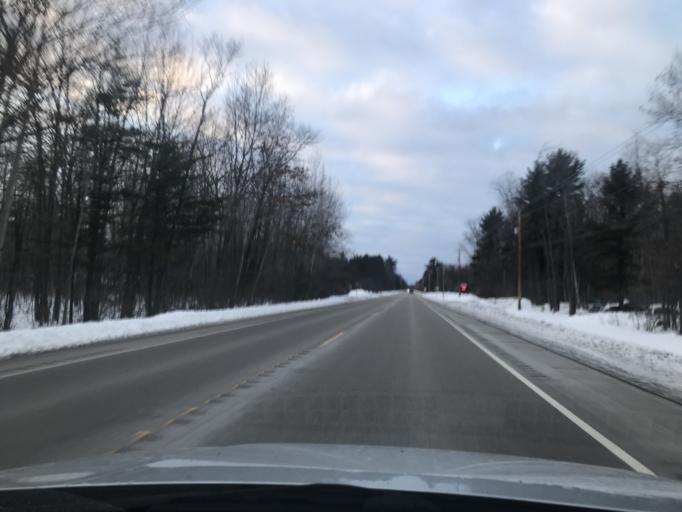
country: US
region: Wisconsin
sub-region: Marinette County
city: Marinette
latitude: 45.1417
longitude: -87.6933
